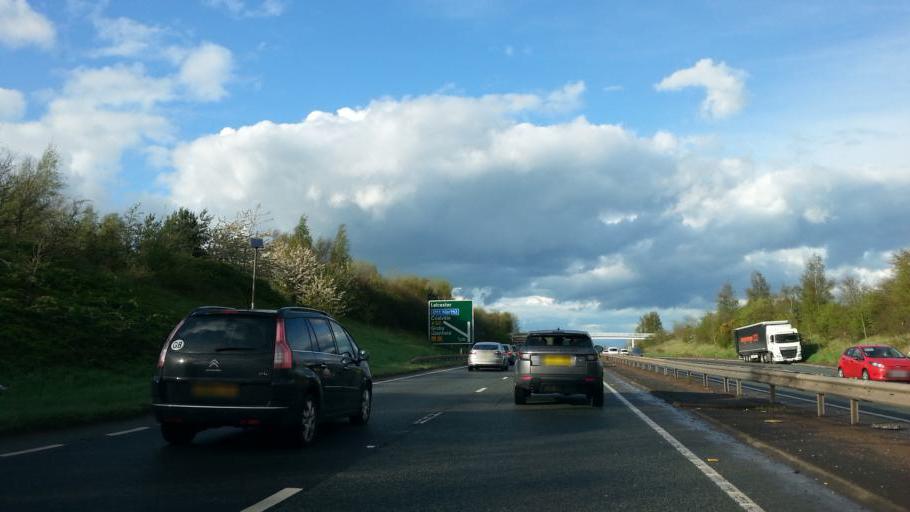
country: GB
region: England
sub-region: Leicestershire
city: Glenfield
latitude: 52.6545
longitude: -1.2182
